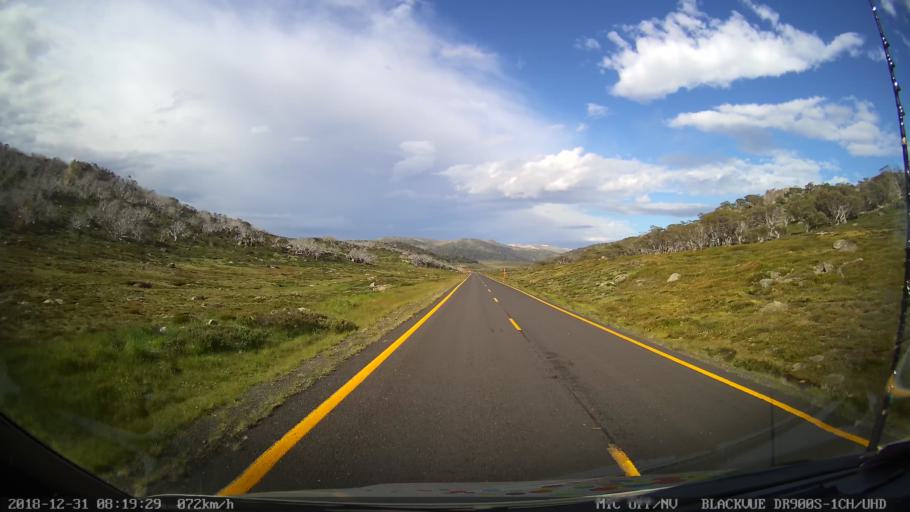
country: AU
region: New South Wales
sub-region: Snowy River
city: Jindabyne
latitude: -36.4194
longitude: 148.3853
